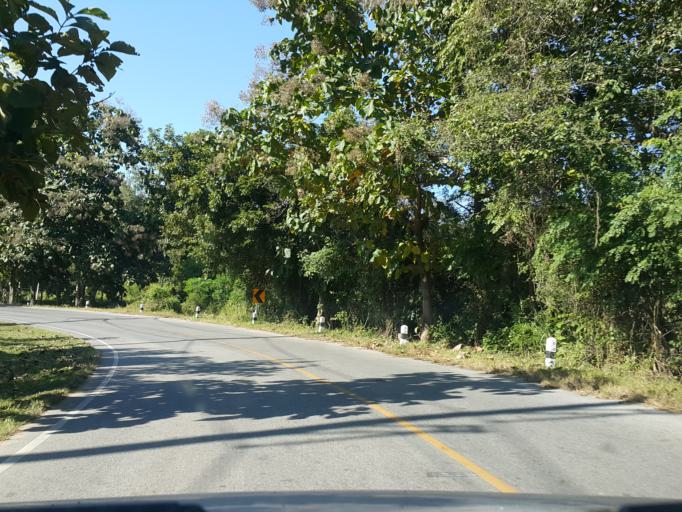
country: TH
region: Mae Hong Son
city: Mae Hi
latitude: 19.2962
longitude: 98.4721
